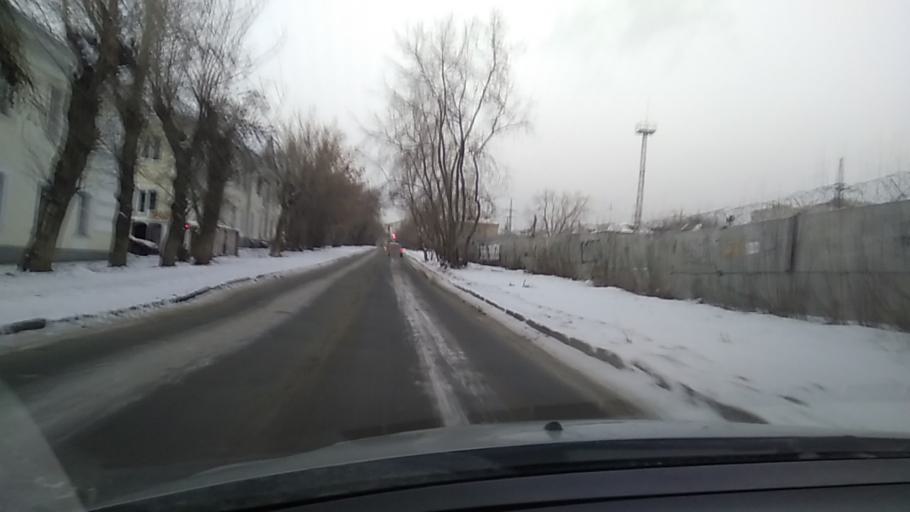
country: RU
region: Sverdlovsk
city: Istok
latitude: 56.7593
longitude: 60.7118
